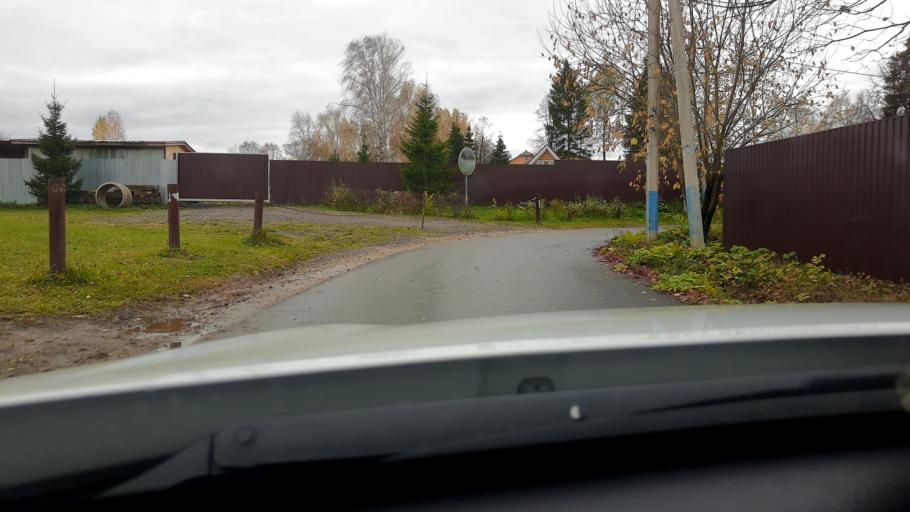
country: RU
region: Moskovskaya
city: Annino
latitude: 55.5581
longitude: 37.2457
